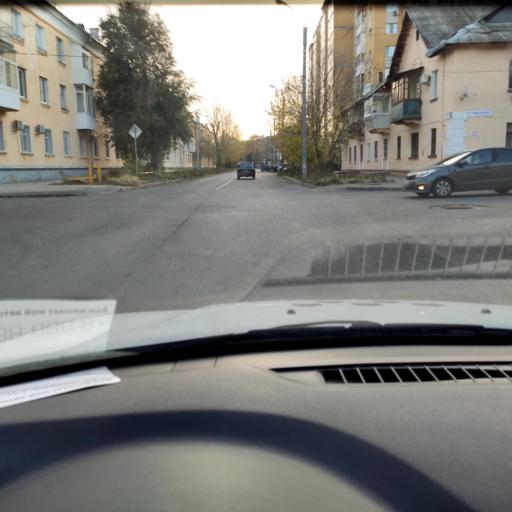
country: RU
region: Samara
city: Tol'yatti
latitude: 53.5040
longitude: 49.3935
